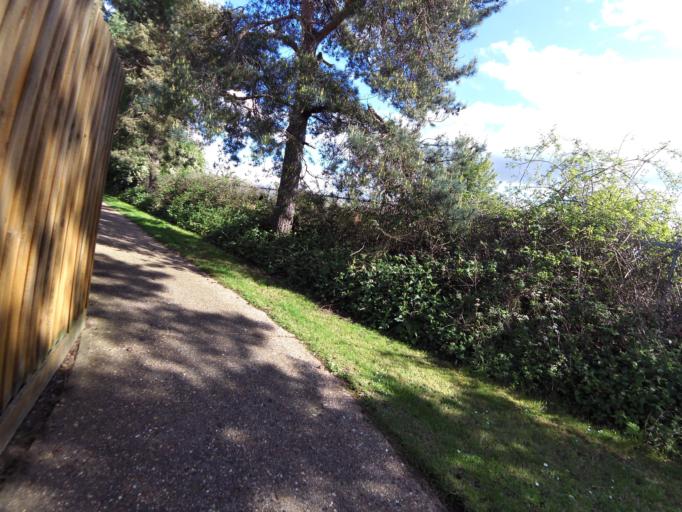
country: GB
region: England
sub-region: Suffolk
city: Thurston
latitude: 52.2494
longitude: 0.8210
